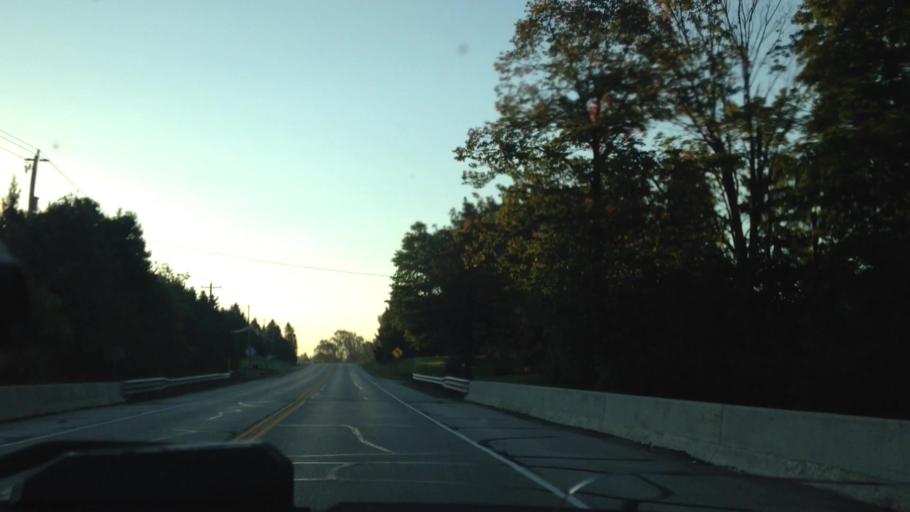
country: US
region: Wisconsin
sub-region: Washington County
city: Newburg
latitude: 43.4249
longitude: -88.0775
